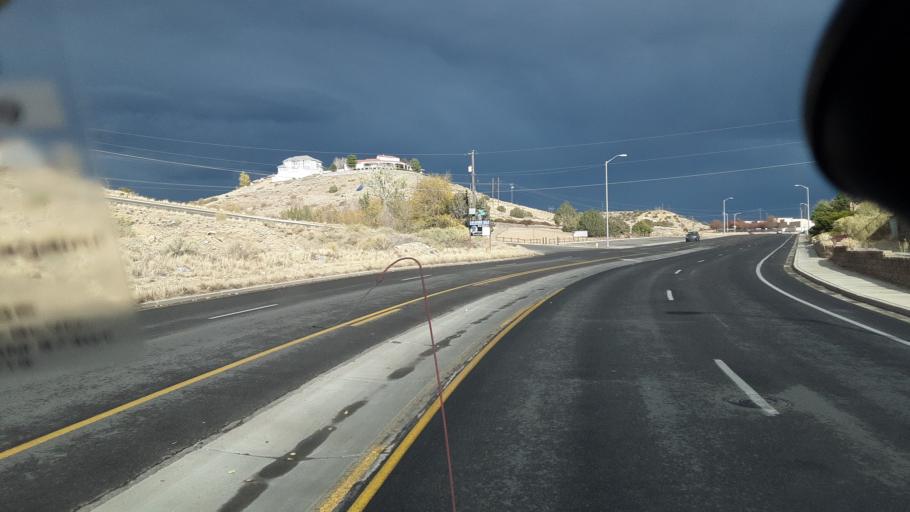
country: US
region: New Mexico
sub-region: San Juan County
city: Farmington
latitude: 36.7611
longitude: -108.1936
